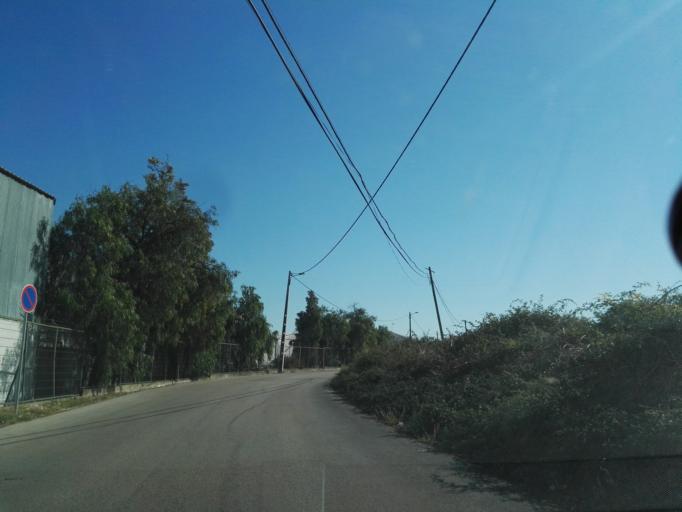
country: PT
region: Lisbon
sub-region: Vila Franca de Xira
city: Sobralinho
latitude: 38.9040
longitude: -9.0250
